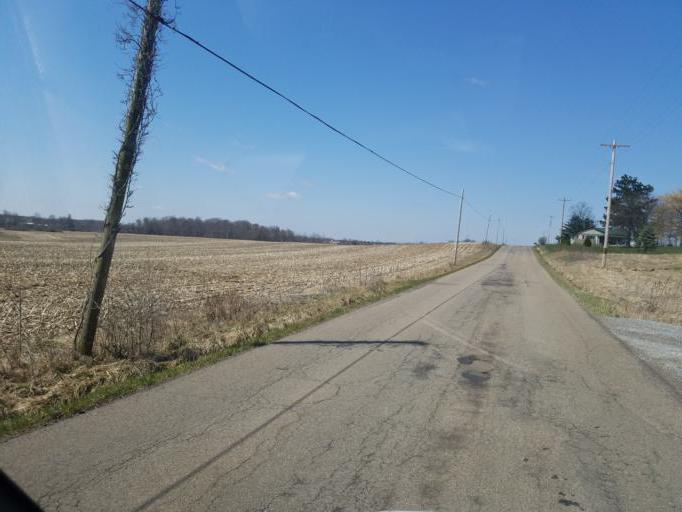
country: US
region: Ohio
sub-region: Knox County
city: Centerburg
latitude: 40.3169
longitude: -82.6448
